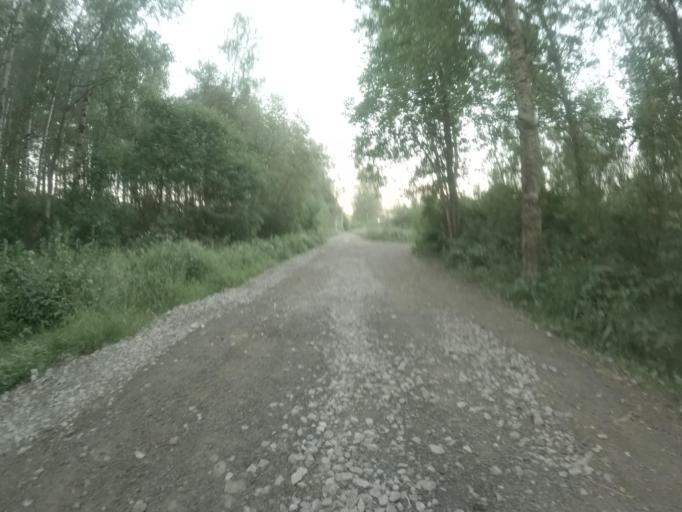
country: RU
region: St.-Petersburg
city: Krasnogvargeisky
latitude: 59.9540
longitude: 30.5053
